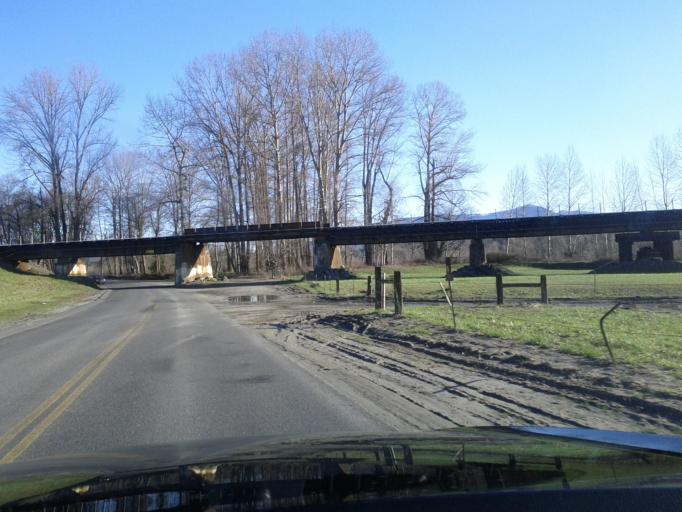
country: US
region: Washington
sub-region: Skagit County
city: Mount Vernon
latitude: 48.4470
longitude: -122.3255
